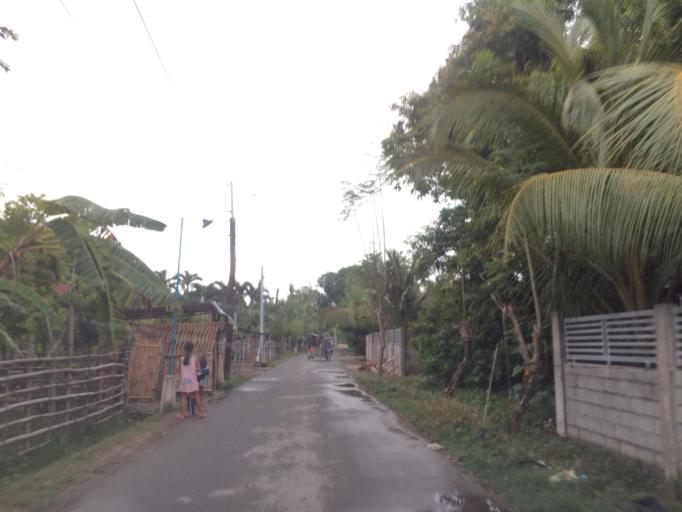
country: PH
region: Ilocos
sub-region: Province of Pangasinan
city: Anambongan
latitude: 15.8728
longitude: 120.3871
